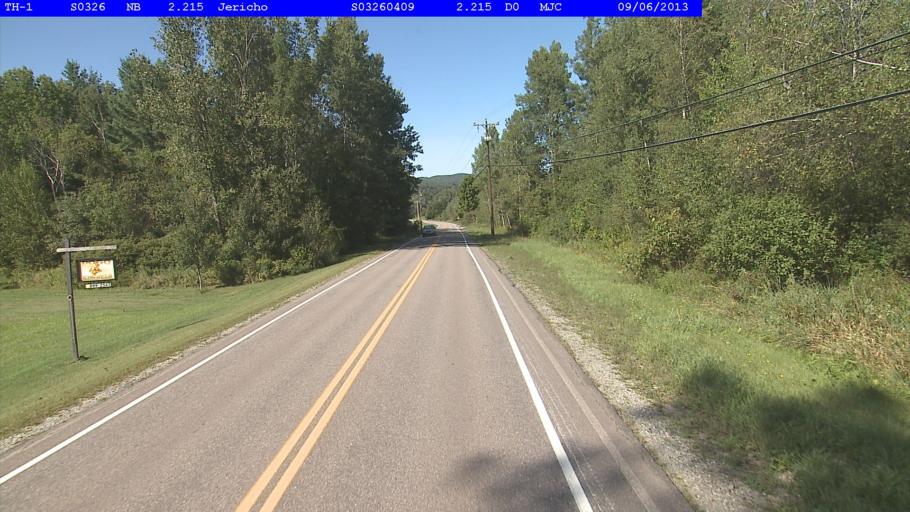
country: US
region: Vermont
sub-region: Chittenden County
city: Jericho
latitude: 44.5084
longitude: -72.9540
